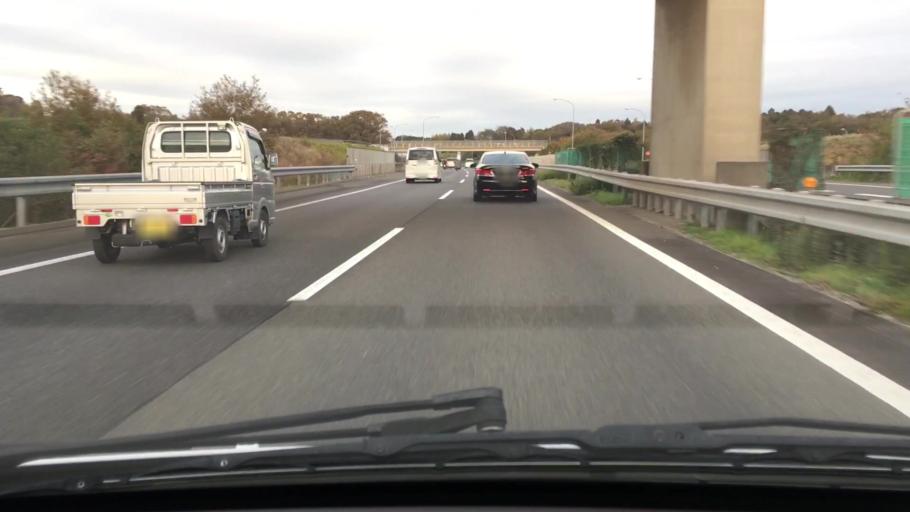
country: JP
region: Chiba
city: Ichihara
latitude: 35.4272
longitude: 140.0416
